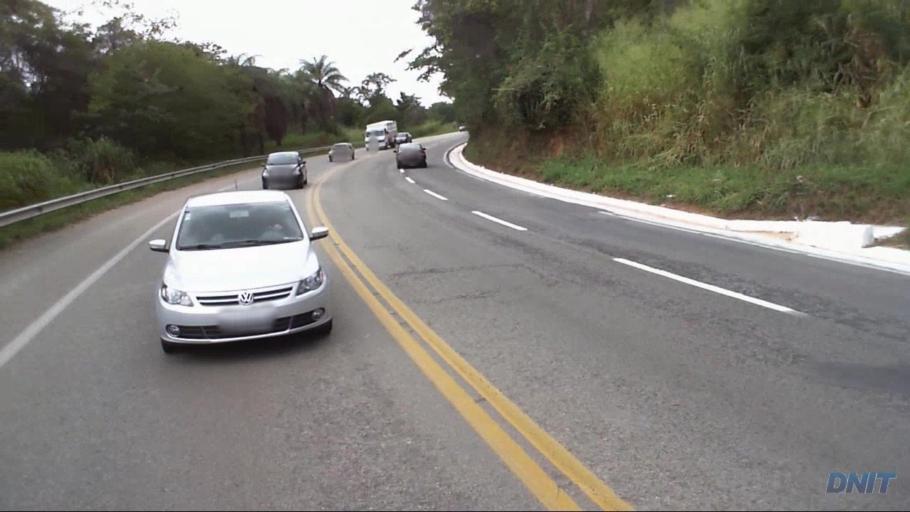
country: BR
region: Minas Gerais
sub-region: Santa Luzia
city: Santa Luzia
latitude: -19.7873
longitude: -43.7428
